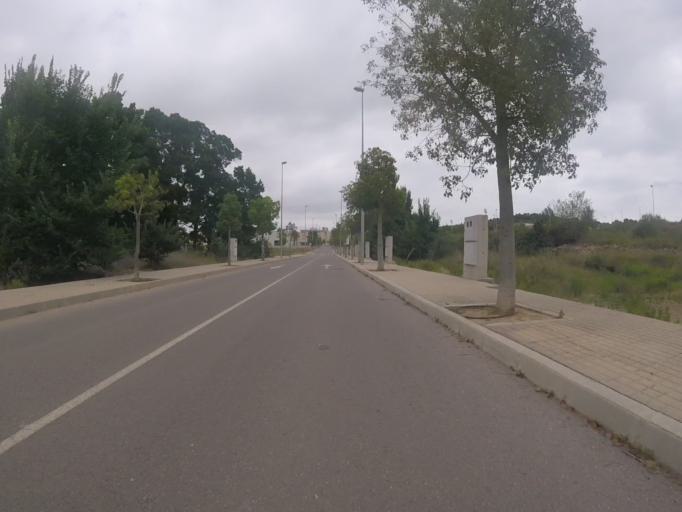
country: ES
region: Valencia
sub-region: Provincia de Castello
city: Cabanes
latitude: 40.1514
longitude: 0.0471
